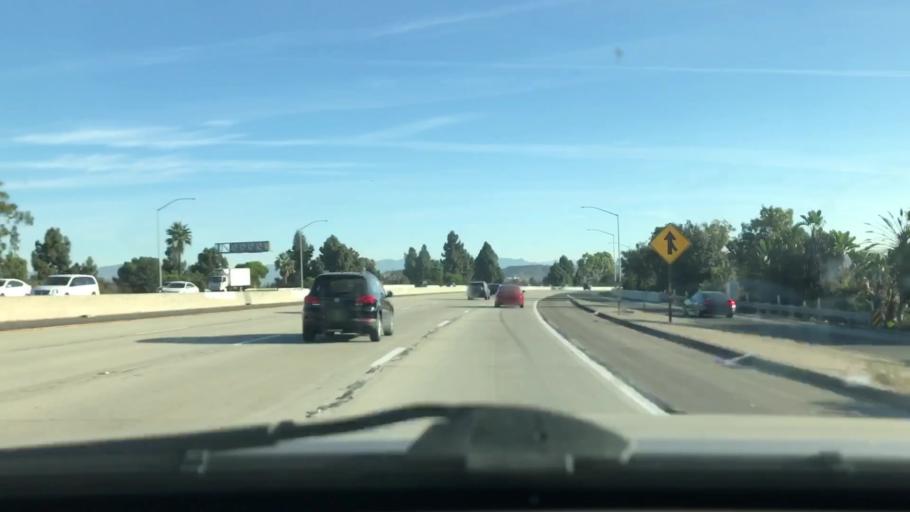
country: US
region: California
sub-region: Los Angeles County
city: Ladera Heights
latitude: 33.9863
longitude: -118.4124
